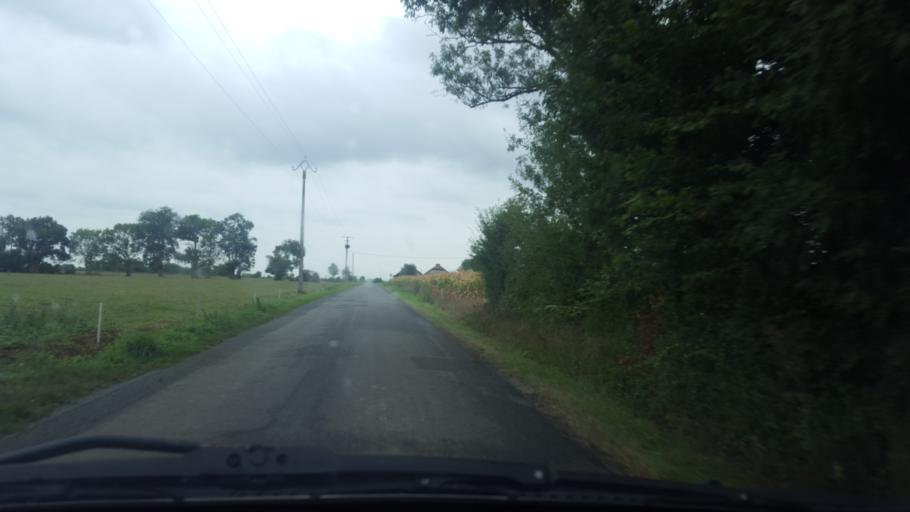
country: FR
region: Pays de la Loire
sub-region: Departement de la Loire-Atlantique
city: Saint-Philbert-de-Grand-Lieu
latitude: 47.0462
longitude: -1.6821
